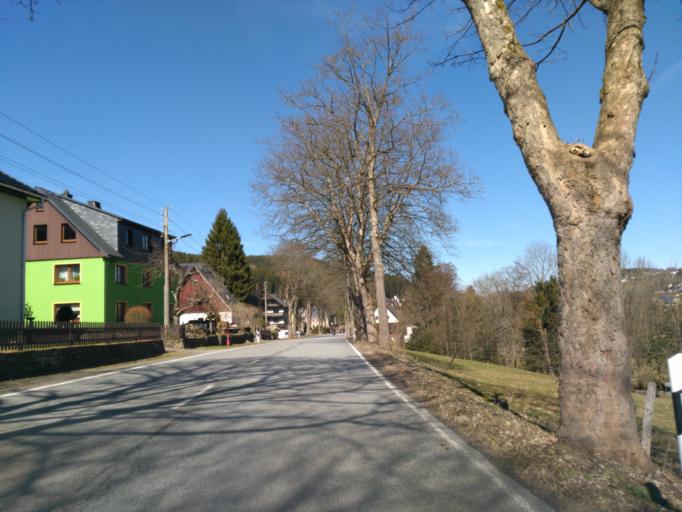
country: DE
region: Saxony
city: Rittersgrun
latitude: 50.4627
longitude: 12.8124
